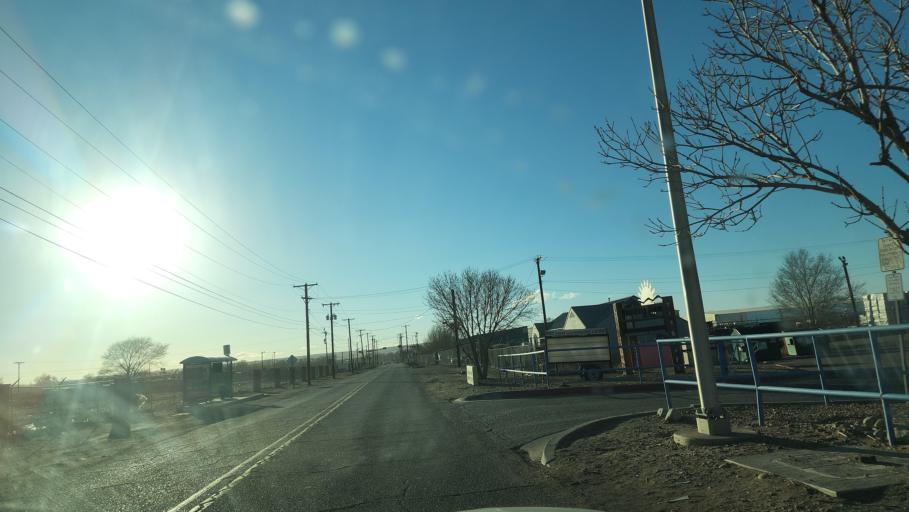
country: US
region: New Mexico
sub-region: Bernalillo County
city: South Valley
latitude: 35.0151
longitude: -106.6577
